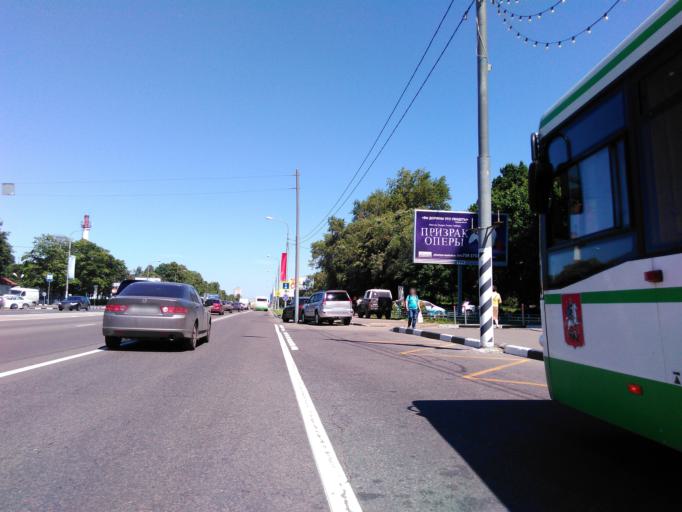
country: RU
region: Moscow
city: Kotlovka
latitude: 55.6707
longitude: 37.5866
